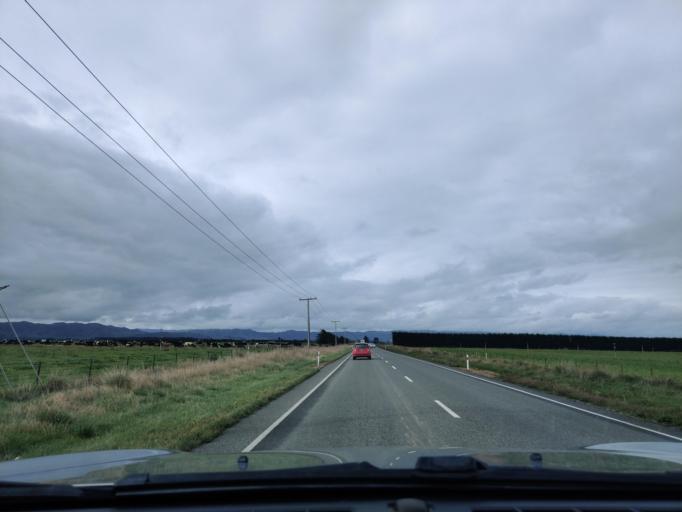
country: NZ
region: Canterbury
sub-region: Hurunui District
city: Amberley
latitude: -42.7330
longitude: 172.8684
